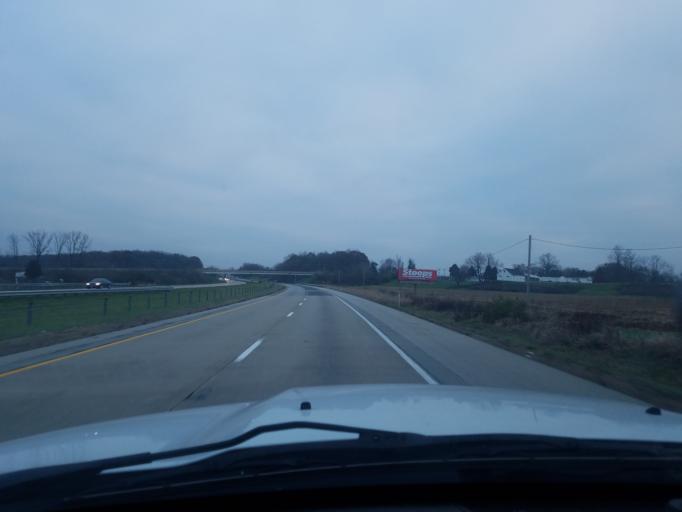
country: US
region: Indiana
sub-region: Madison County
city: Chesterfield
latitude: 40.0603
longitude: -85.5949
